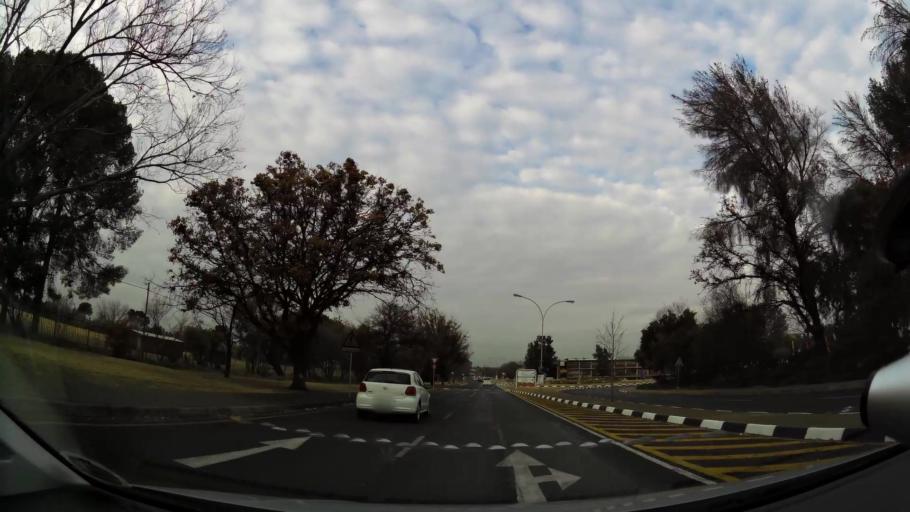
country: ZA
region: Orange Free State
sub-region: Mangaung Metropolitan Municipality
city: Bloemfontein
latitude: -29.1110
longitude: 26.1917
